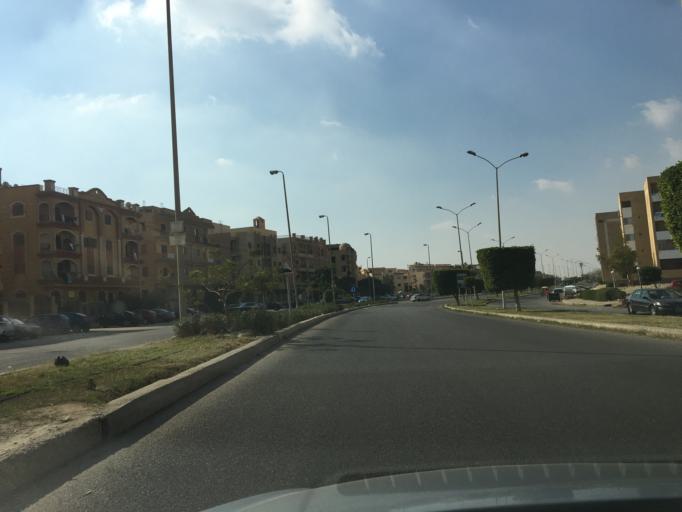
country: EG
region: Al Jizah
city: Awsim
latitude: 30.0420
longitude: 30.9733
